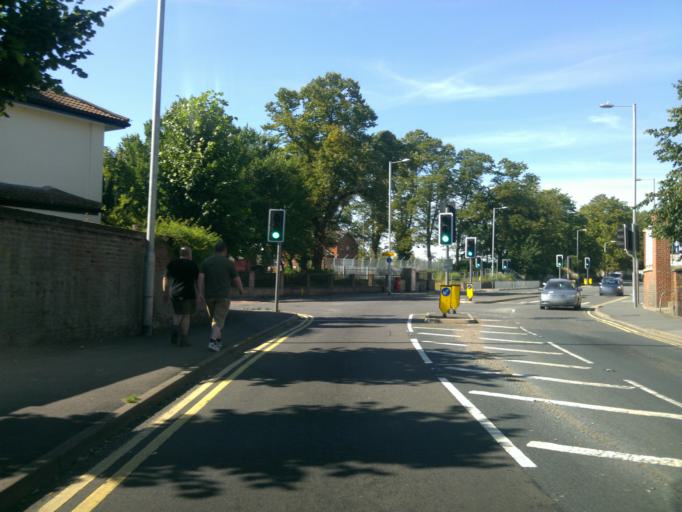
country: GB
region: England
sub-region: Essex
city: Colchester
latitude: 51.8800
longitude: 0.9044
